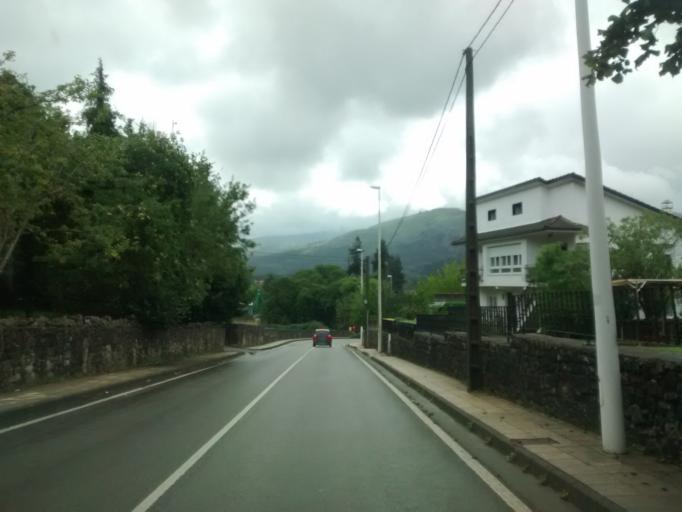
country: ES
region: Cantabria
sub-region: Provincia de Cantabria
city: Entrambasaguas
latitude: 43.3539
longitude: -3.7031
